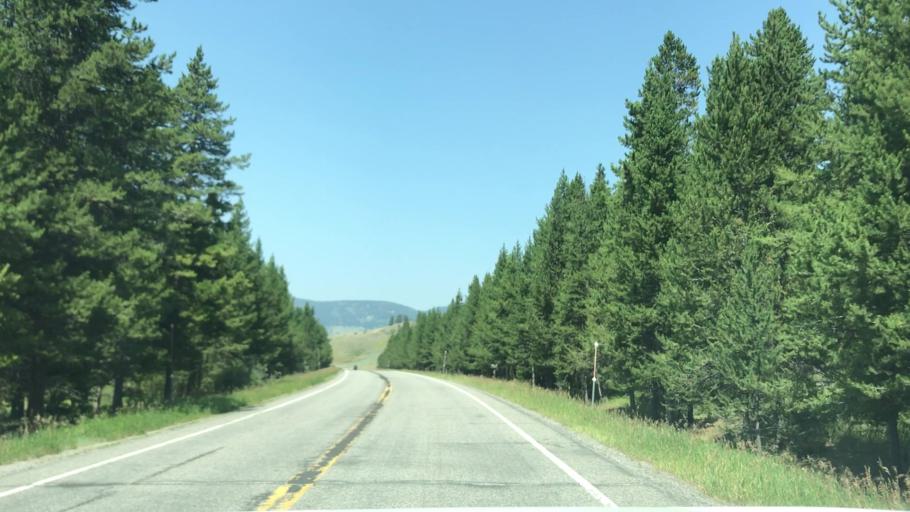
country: US
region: Montana
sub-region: Gallatin County
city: Big Sky
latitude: 45.0343
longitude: -111.1134
